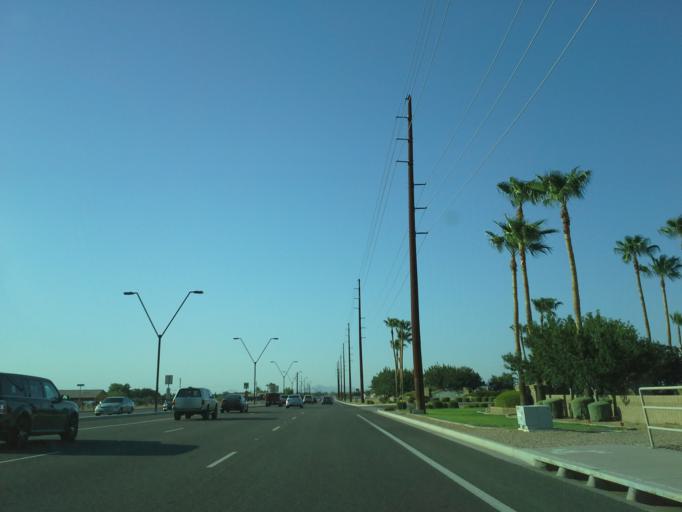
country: US
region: Arizona
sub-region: Maricopa County
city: Queen Creek
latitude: 33.2079
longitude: -111.6343
